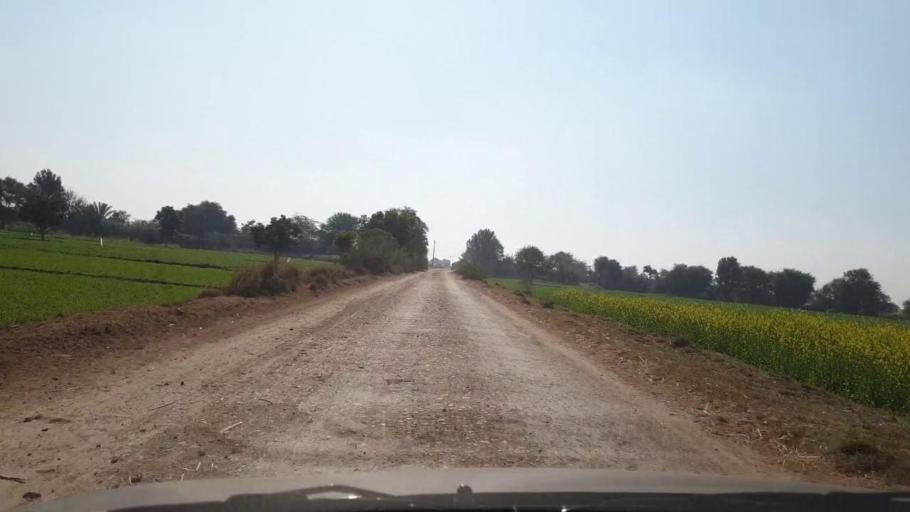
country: PK
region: Sindh
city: Jhol
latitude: 25.9396
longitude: 68.7997
